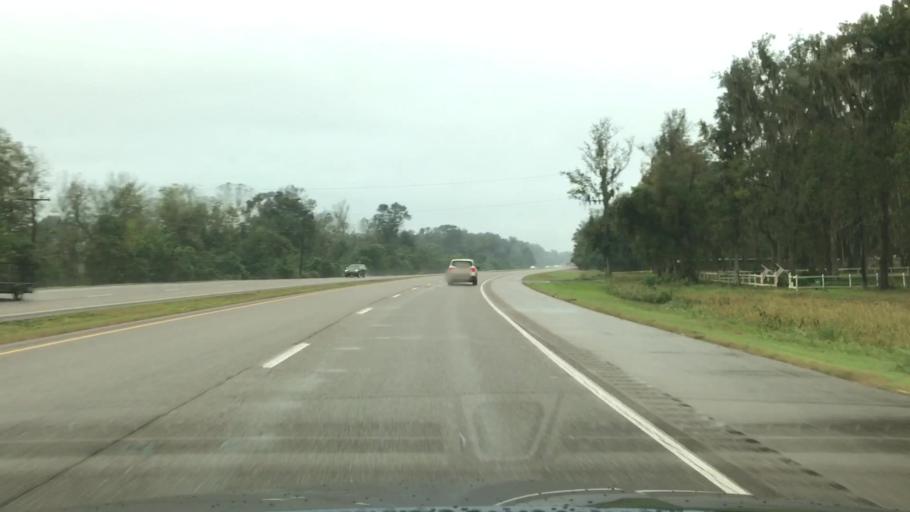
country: US
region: Louisiana
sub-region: Saint Charles Parish
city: Des Allemands
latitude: 29.8435
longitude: -90.4483
